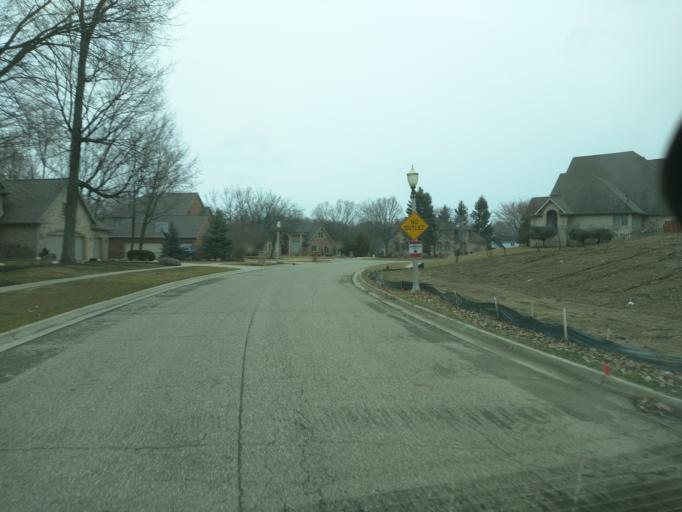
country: US
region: Michigan
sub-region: Eaton County
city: Waverly
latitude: 42.7607
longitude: -84.6341
